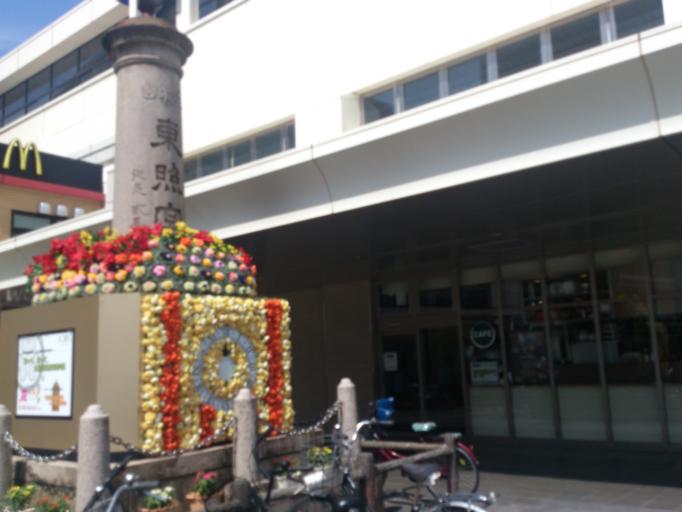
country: JP
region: Shizuoka
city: Shizuoka-shi
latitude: 34.9713
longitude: 138.3891
